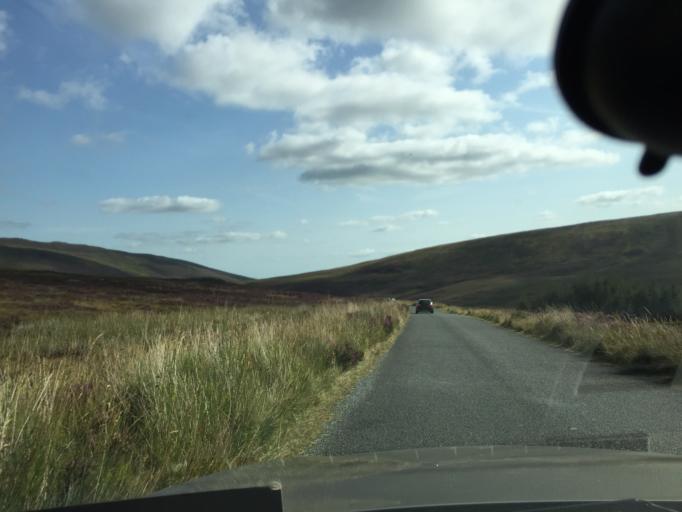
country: IE
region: Leinster
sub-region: Wicklow
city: Rathdrum
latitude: 53.0750
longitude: -6.3532
